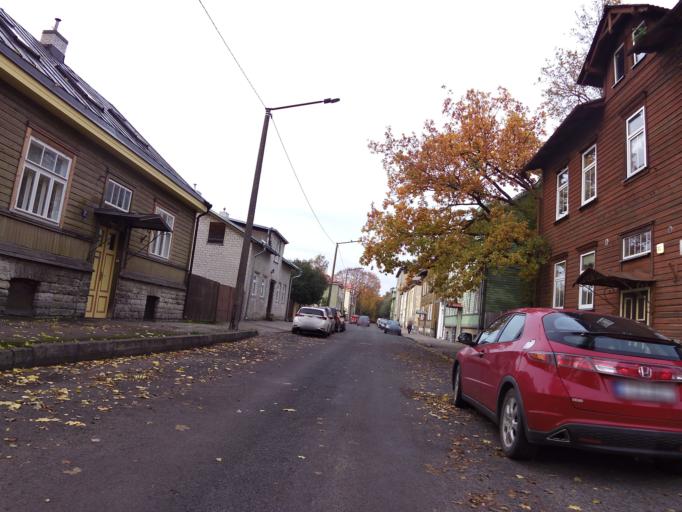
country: EE
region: Harju
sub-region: Tallinna linn
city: Tallinn
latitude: 59.4389
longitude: 24.7142
